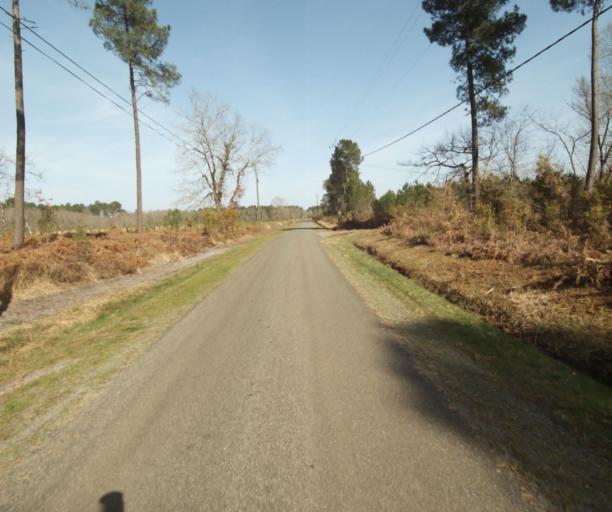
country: FR
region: Aquitaine
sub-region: Departement des Landes
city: Roquefort
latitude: 44.1436
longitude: -0.2398
